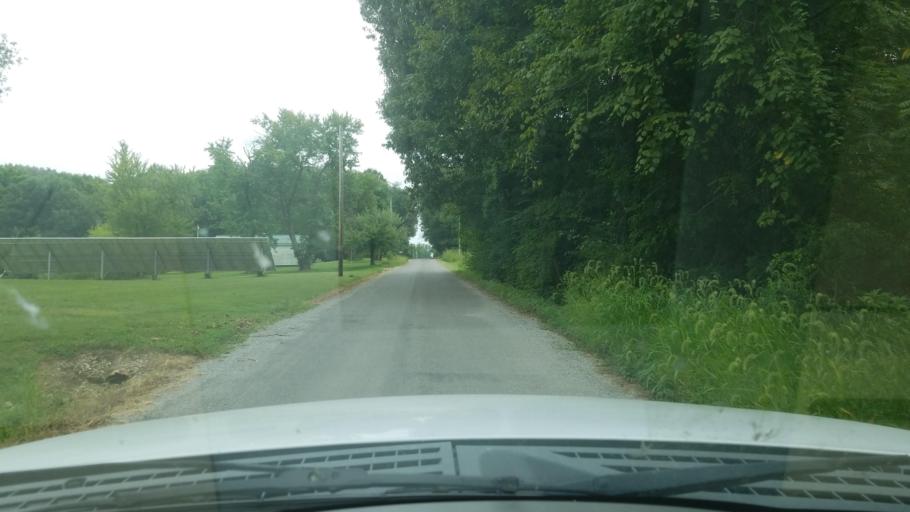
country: US
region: Illinois
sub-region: Saline County
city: Eldorado
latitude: 37.8281
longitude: -88.4478
